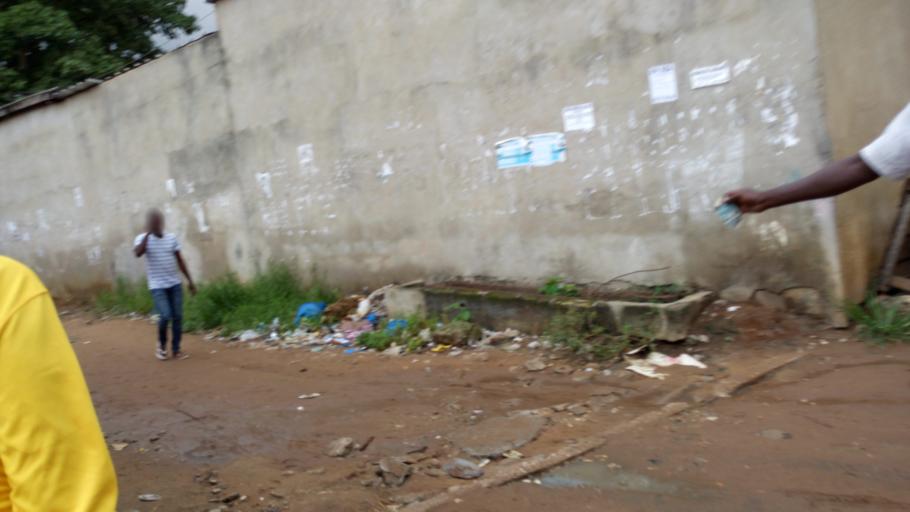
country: CI
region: Lagunes
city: Abobo
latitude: 5.4058
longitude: -3.9973
